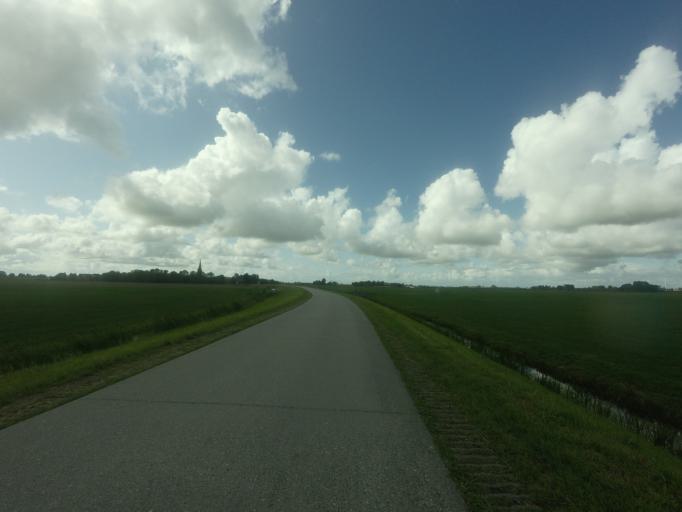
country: NL
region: Friesland
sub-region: Sudwest Fryslan
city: Scharnegoutum
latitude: 53.0780
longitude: 5.6440
